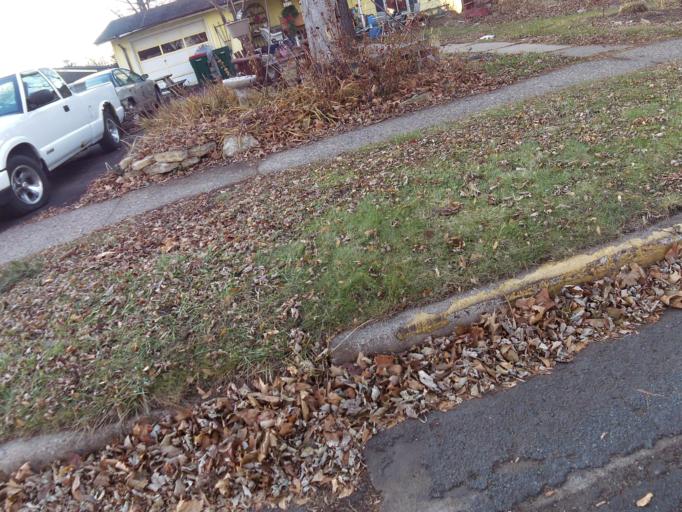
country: US
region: Wisconsin
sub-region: Pierce County
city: River Falls
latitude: 44.8597
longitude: -92.6167
